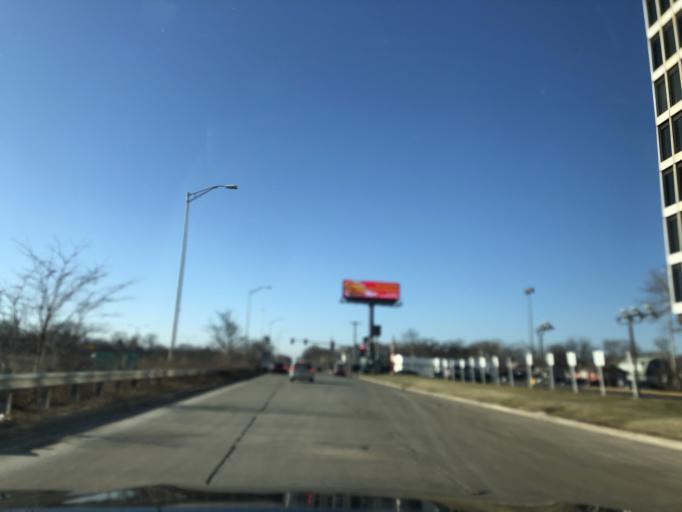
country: US
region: Illinois
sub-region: Cook County
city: Maywood
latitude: 41.8718
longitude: -87.8321
